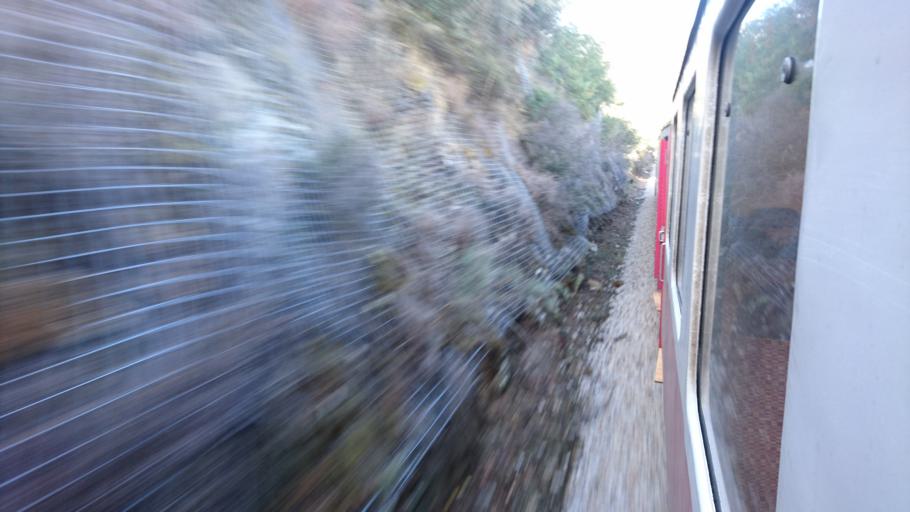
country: PT
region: Guarda
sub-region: Vila Nova de Foz Coa
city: Vila Nova de Foz Coa
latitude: 41.1241
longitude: -7.1870
